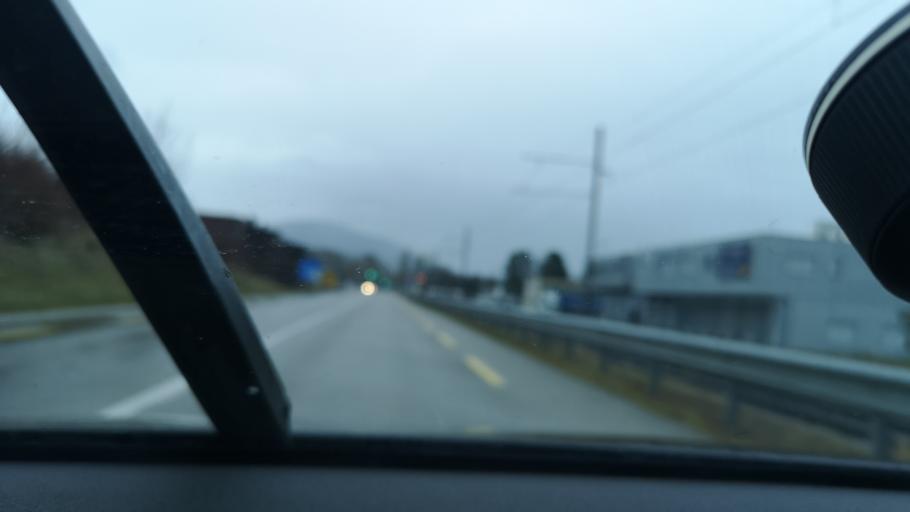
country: CH
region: Neuchatel
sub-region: Boudry District
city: Cortaillod
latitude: 46.9593
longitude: 6.8616
